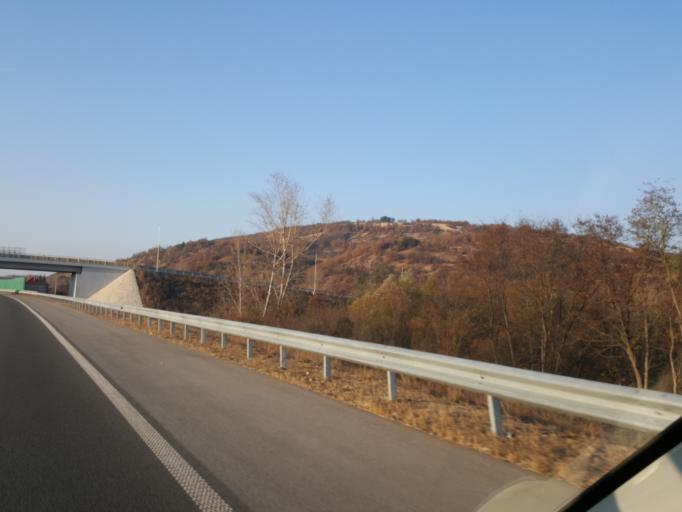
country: RS
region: Central Serbia
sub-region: Pirotski Okrug
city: Dimitrovgrad
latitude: 43.0439
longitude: 22.7078
